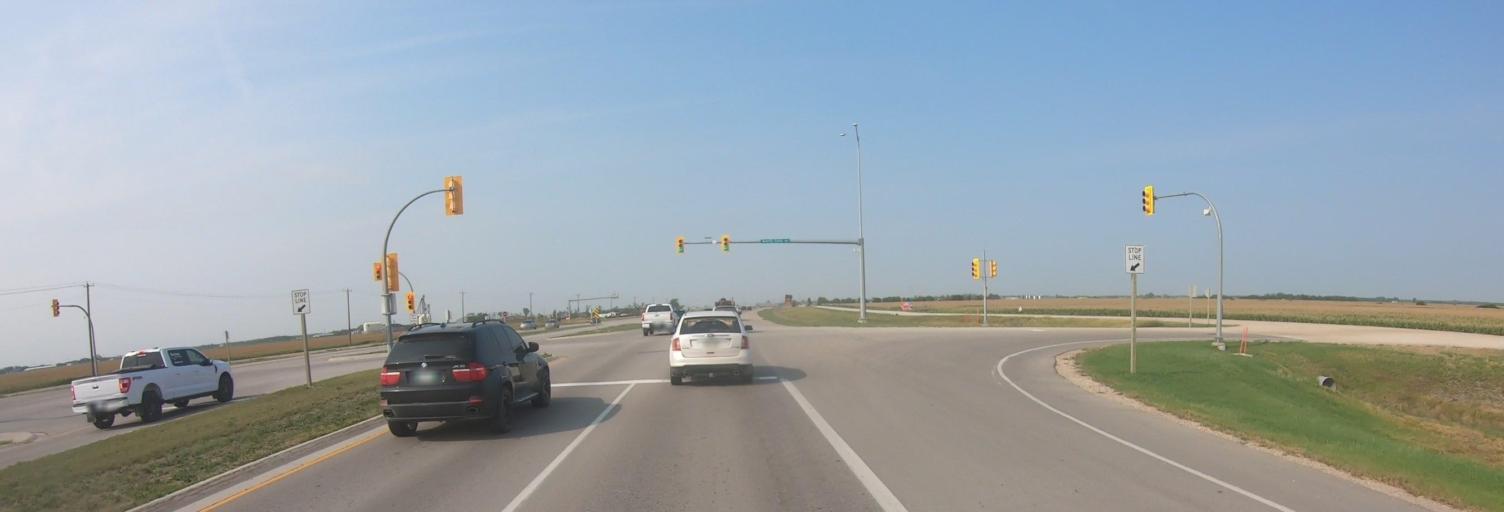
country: CA
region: Manitoba
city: Steinbach
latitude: 49.5670
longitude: -96.6877
